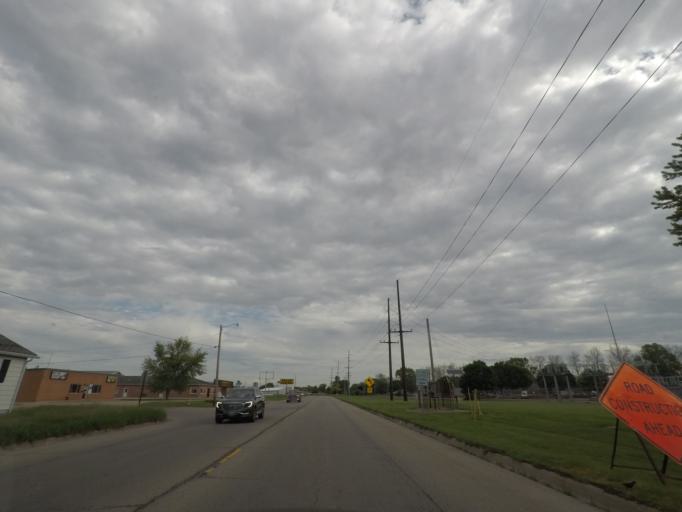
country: US
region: Illinois
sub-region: Logan County
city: Lincoln
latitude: 40.1443
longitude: -89.3488
